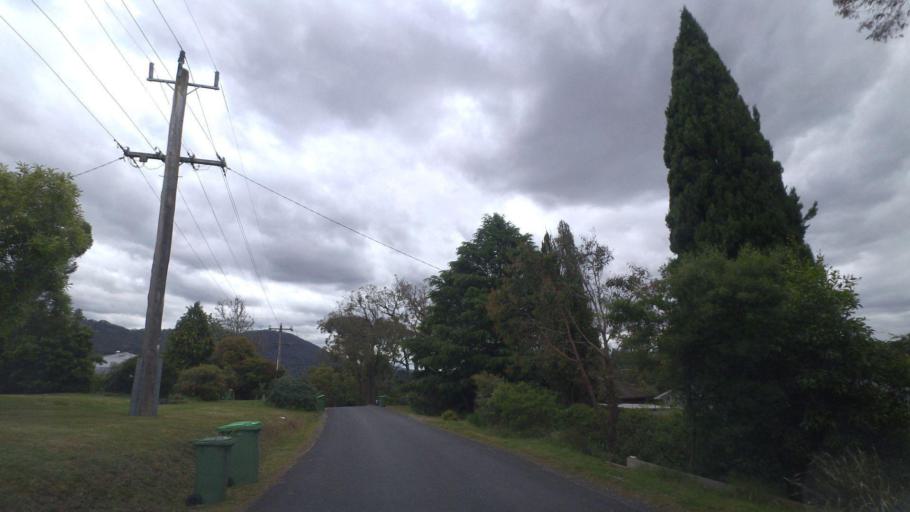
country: AU
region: Victoria
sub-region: Yarra Ranges
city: Mount Evelyn
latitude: -37.7881
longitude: 145.3654
